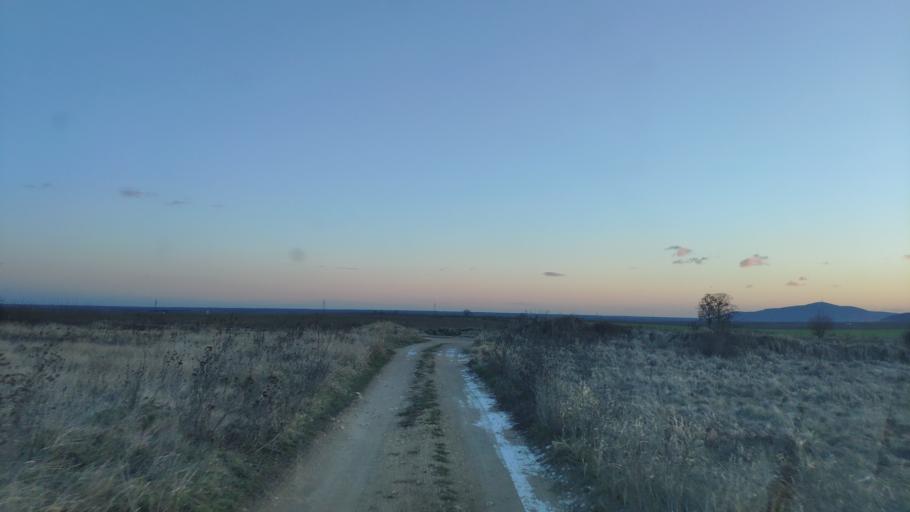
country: HU
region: Borsod-Abauj-Zemplen
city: Olaszliszka
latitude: 48.2669
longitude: 21.4014
